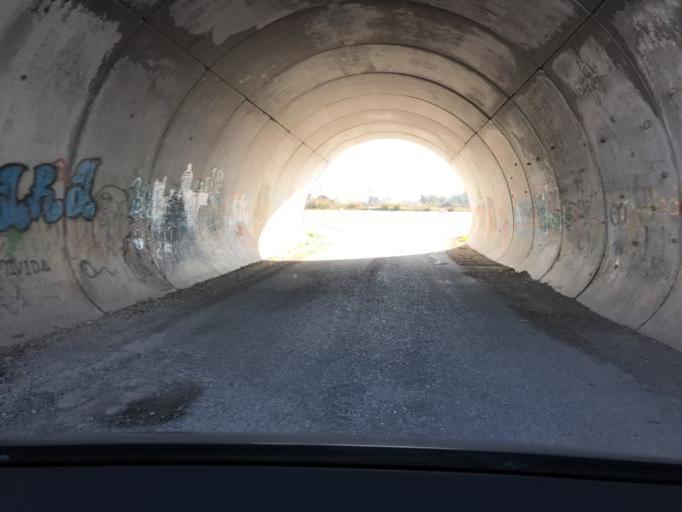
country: ES
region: Andalusia
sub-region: Provincia de Granada
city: Alhendin
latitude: 37.1115
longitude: -3.6311
